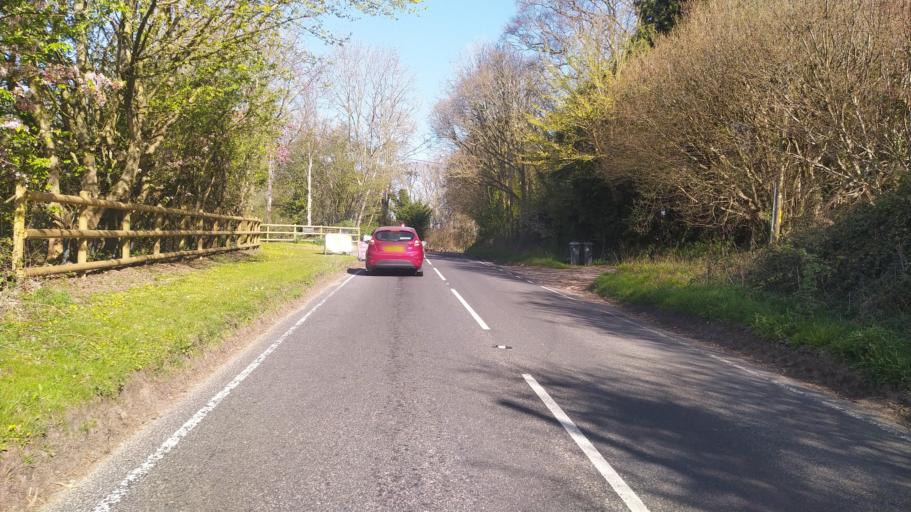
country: GB
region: England
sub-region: Dorset
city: Wimborne Minster
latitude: 50.8350
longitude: -1.9970
